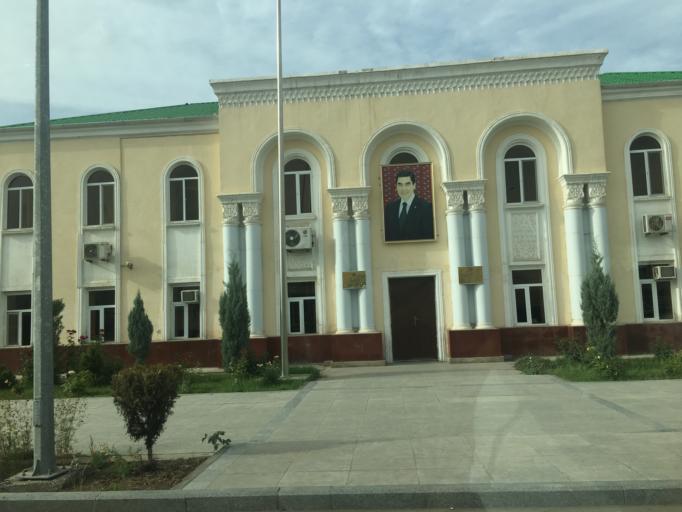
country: TM
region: Mary
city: Mary
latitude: 37.5890
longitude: 61.8387
